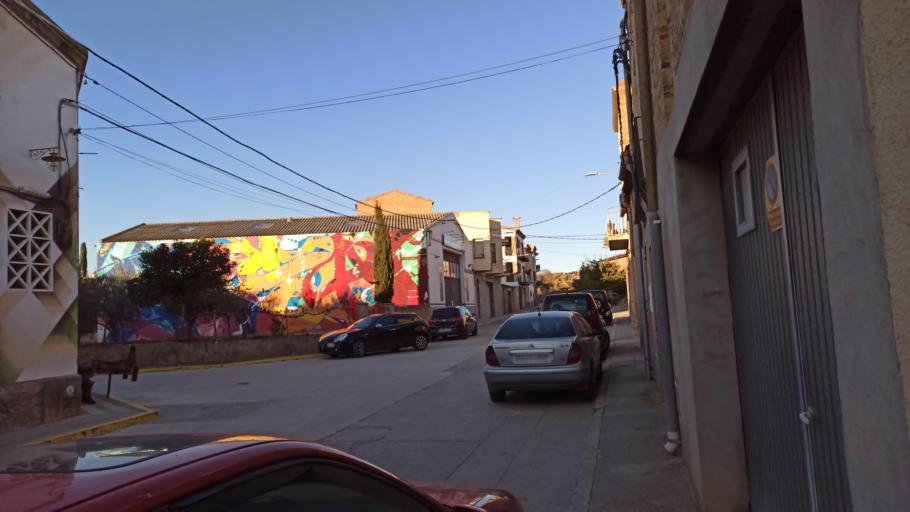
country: ES
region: Catalonia
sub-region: Provincia de Lleida
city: Penelles
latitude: 41.7582
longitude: 0.9662
